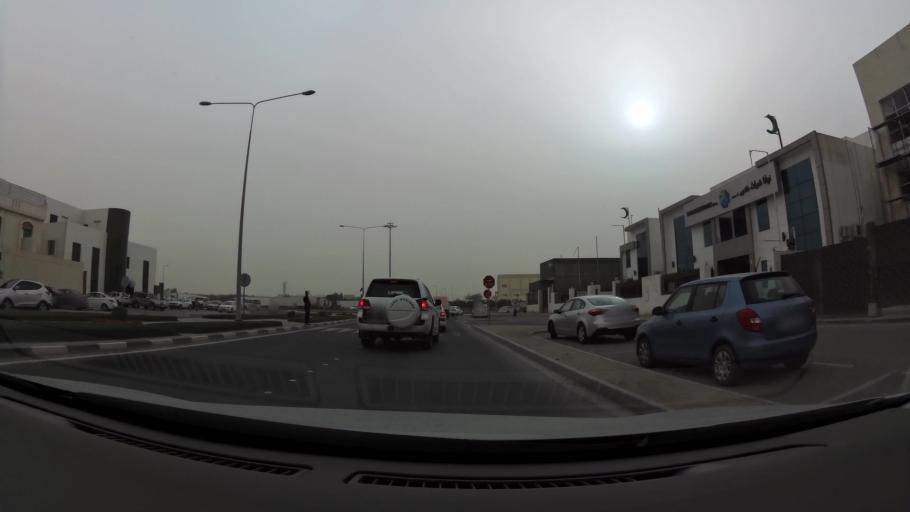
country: QA
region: Baladiyat ad Dawhah
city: Doha
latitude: 25.2471
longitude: 51.4798
